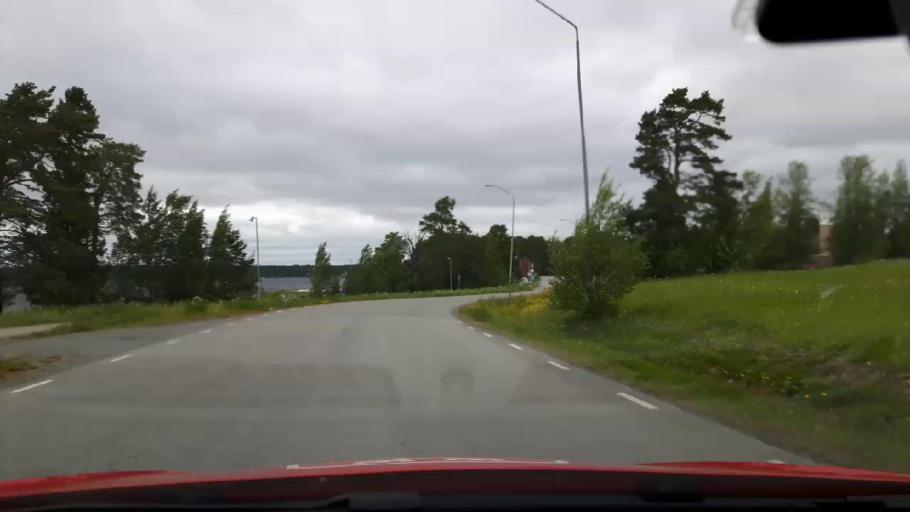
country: SE
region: Jaemtland
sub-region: OEstersunds Kommun
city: Ostersund
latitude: 63.1899
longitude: 14.6314
